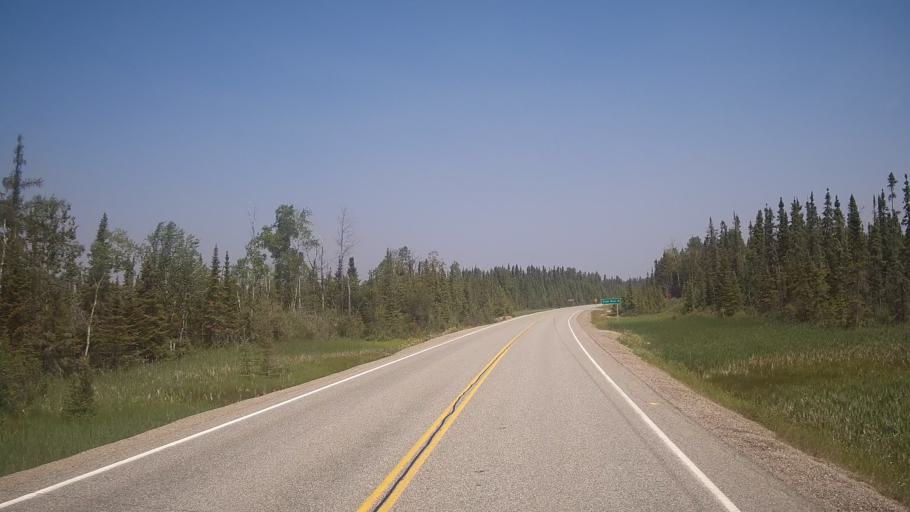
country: CA
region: Ontario
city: Timmins
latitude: 48.1906
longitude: -81.5835
